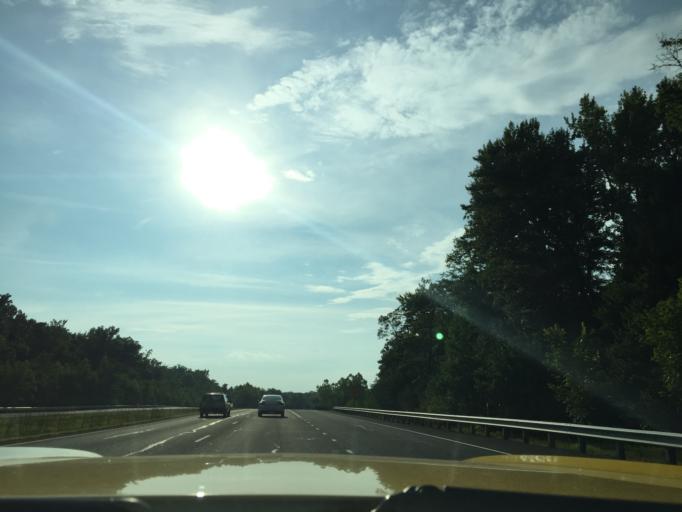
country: US
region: Virginia
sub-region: Fairfax County
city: Newington
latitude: 38.7224
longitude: -77.1781
